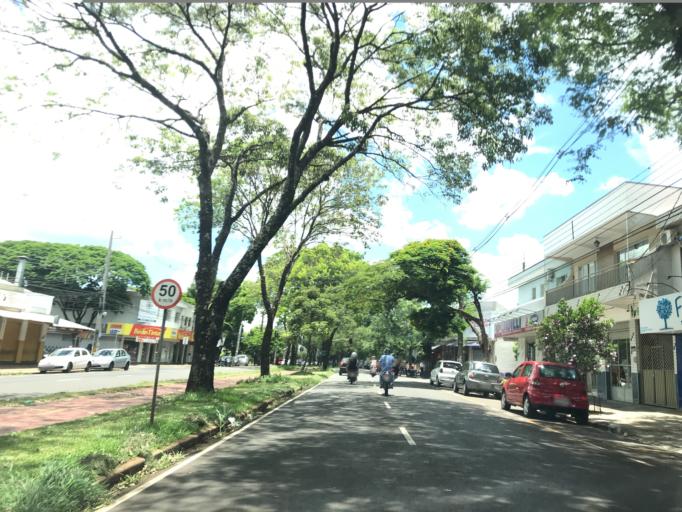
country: BR
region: Parana
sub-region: Maringa
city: Maringa
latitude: -23.4053
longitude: -51.9222
